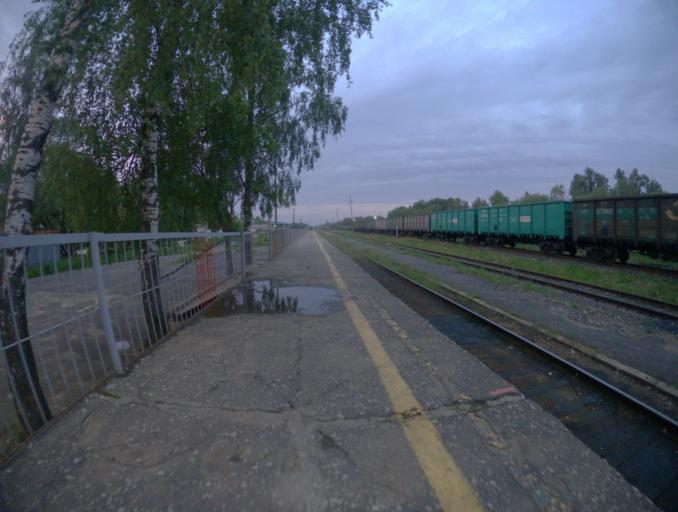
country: RU
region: Vladimir
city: Gus'-Khrustal'nyy
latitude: 55.6181
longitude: 40.6503
